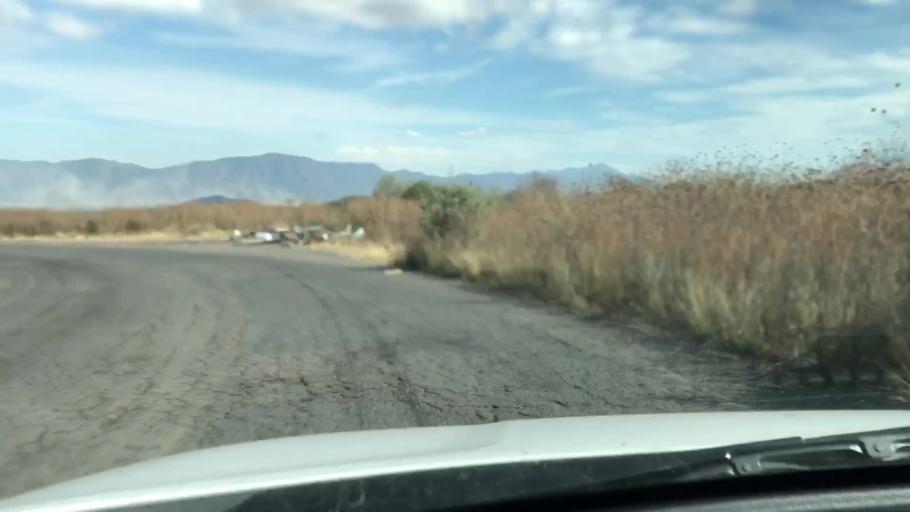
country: MX
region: Jalisco
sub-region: Zacoalco de Torres
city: Barranca de Otates (Barranca de Otatan)
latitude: 20.2445
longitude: -103.6691
